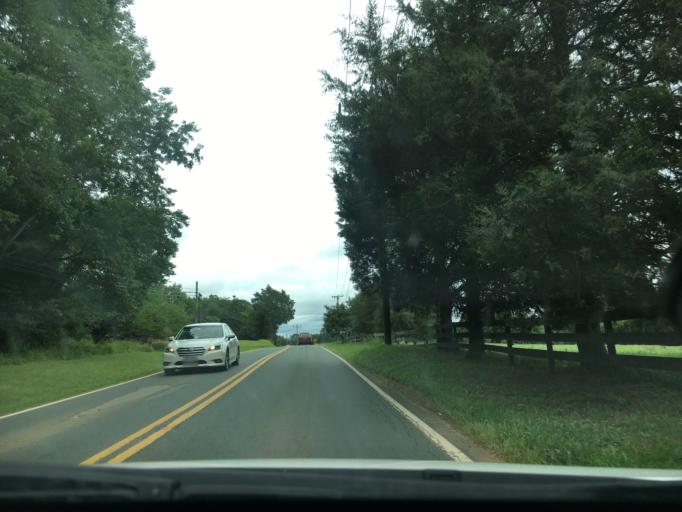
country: US
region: Virginia
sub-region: City of Charlottesville
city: Charlottesville
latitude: 37.9944
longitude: -78.4496
